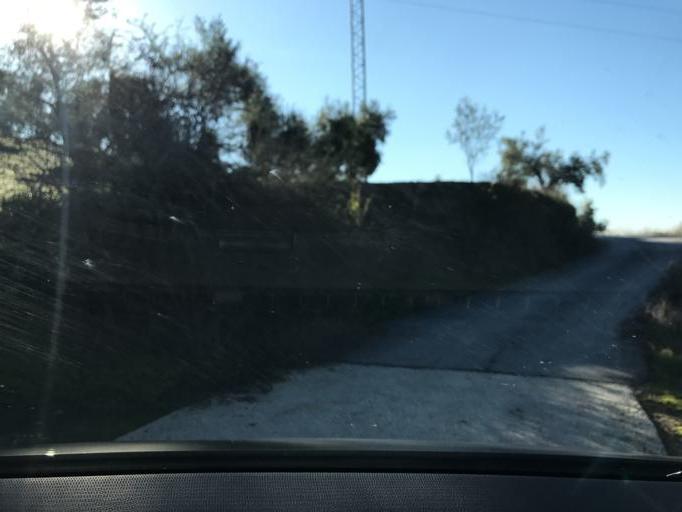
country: ES
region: Andalusia
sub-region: Provincia de Granada
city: Peligros
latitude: 37.2416
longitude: -3.6339
